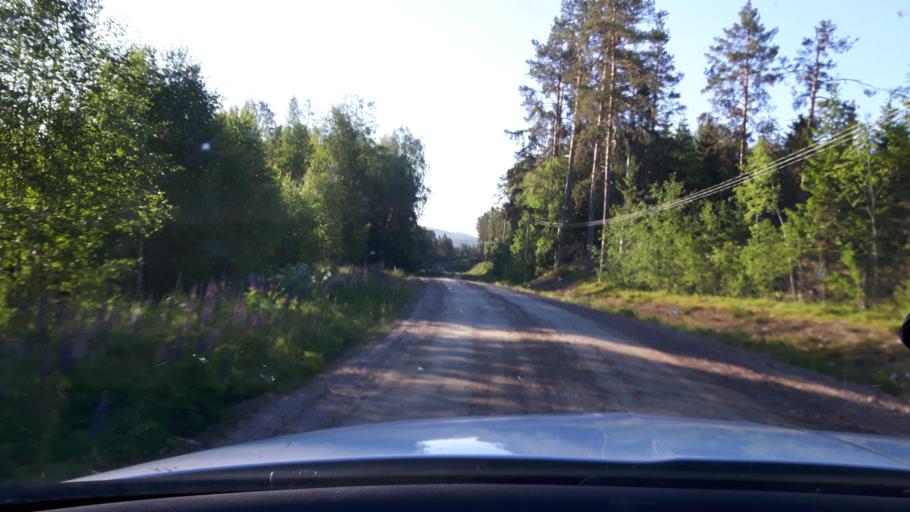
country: SE
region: Vaesternorrland
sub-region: Ange Kommun
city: Ange
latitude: 62.1685
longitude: 15.6486
